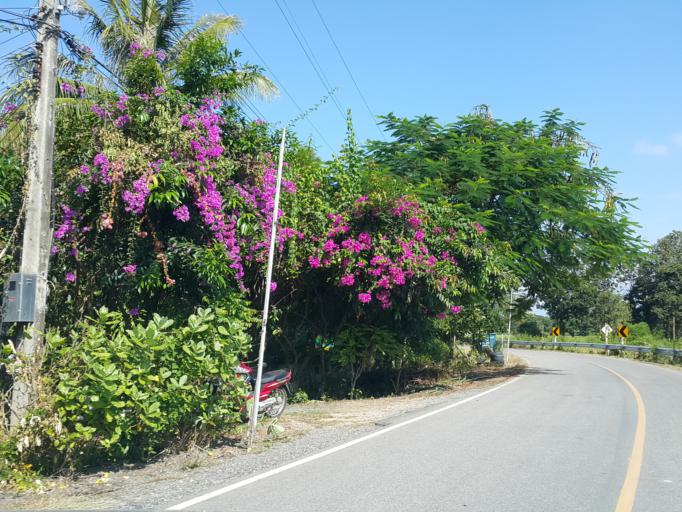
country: TH
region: Chiang Mai
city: Mae On
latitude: 18.8045
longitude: 99.1847
